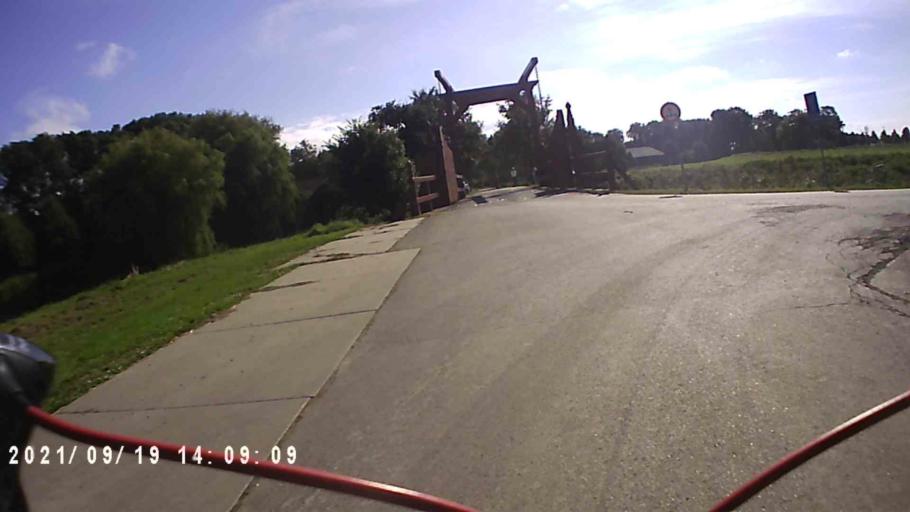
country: NL
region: Groningen
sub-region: Gemeente  Oldambt
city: Winschoten
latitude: 53.1396
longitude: 7.1371
